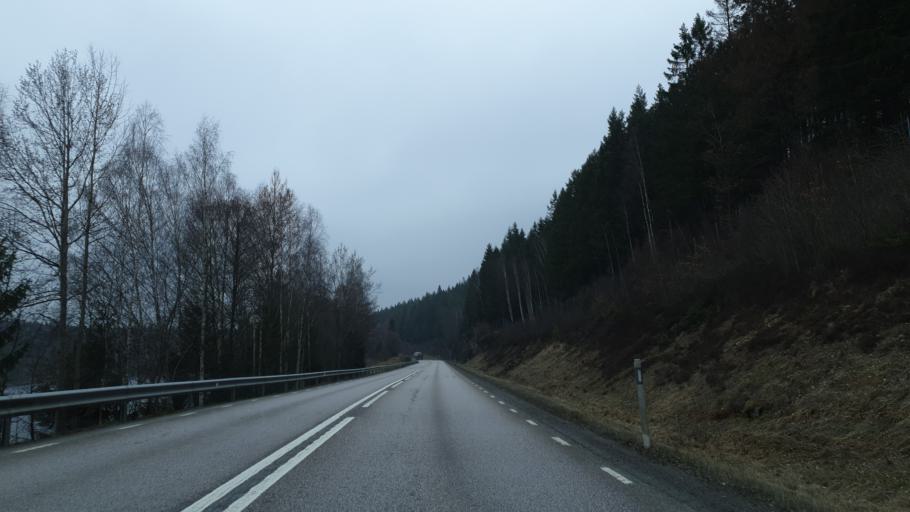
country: SE
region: Vaestra Goetaland
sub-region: Harryda Kommun
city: Hindas
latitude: 57.6278
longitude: 12.4133
